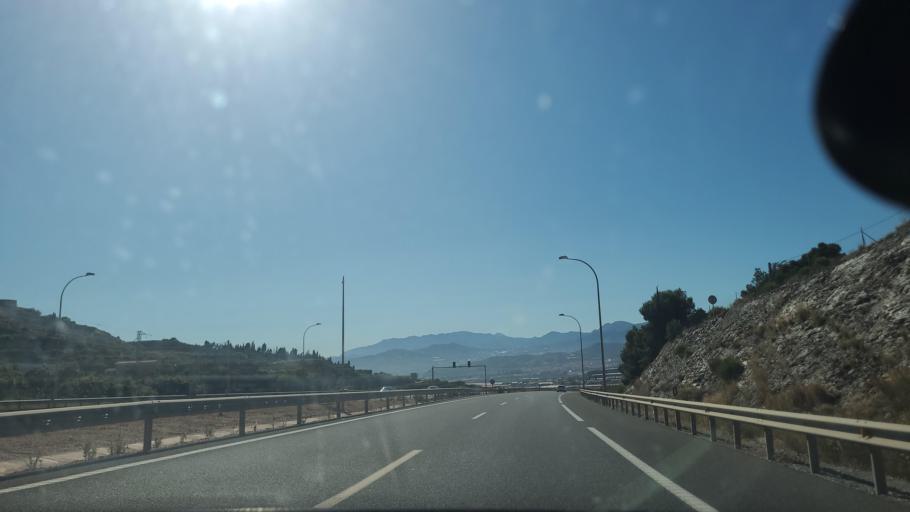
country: ES
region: Andalusia
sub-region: Provincia de Granada
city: El Varadero
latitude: 36.7176
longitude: -3.4591
